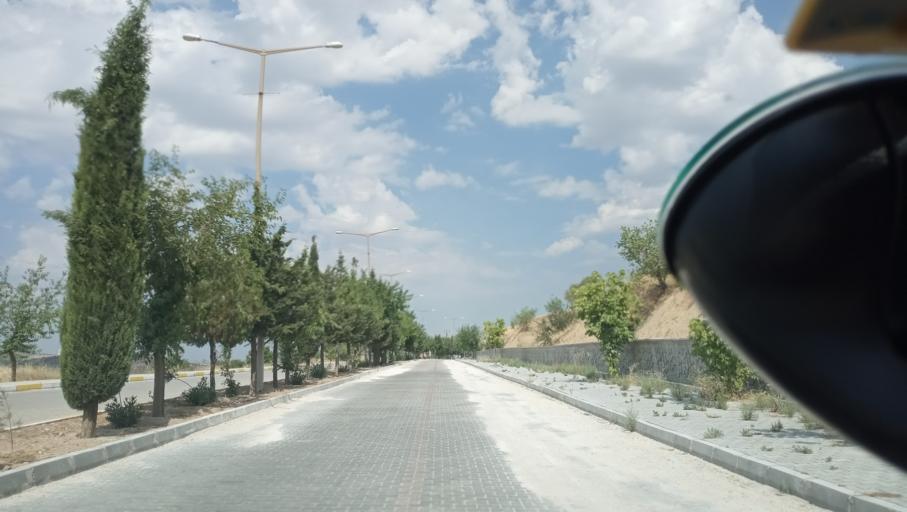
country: TR
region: Mardin
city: Kabala
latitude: 37.3422
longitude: 40.8081
